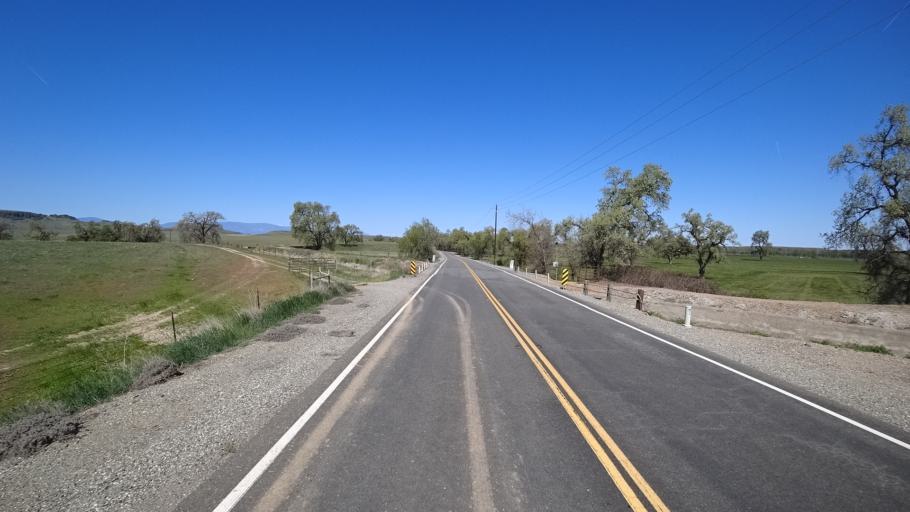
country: US
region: California
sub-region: Glenn County
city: Orland
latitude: 39.7915
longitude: -122.3112
